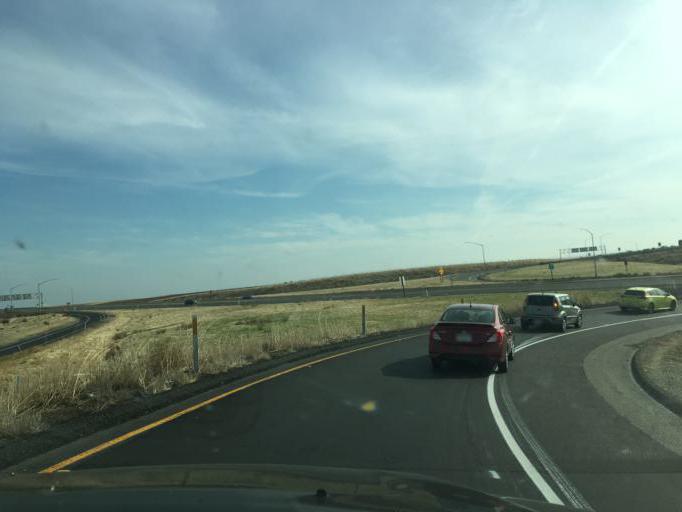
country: US
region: California
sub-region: Merced County
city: Los Banos
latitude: 37.0576
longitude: -120.9690
